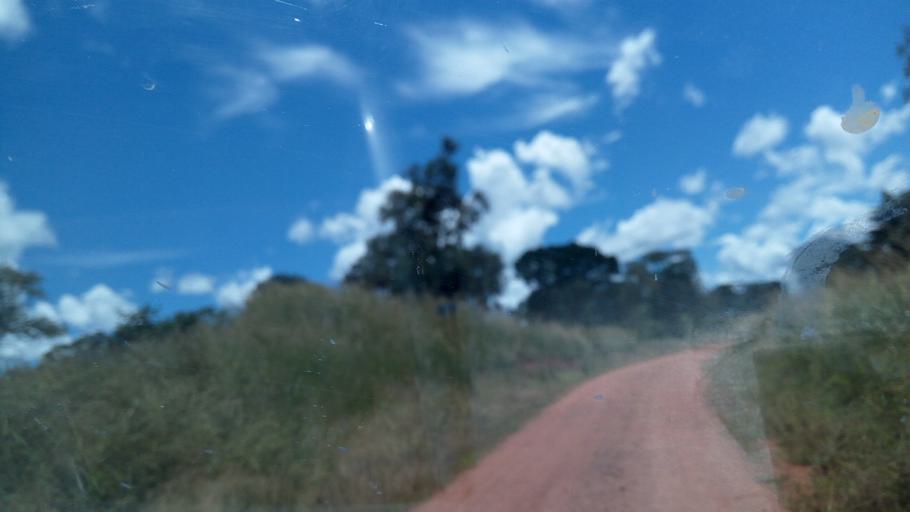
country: CD
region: Katanga
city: Kalemie
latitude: -5.4270
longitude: 28.9376
